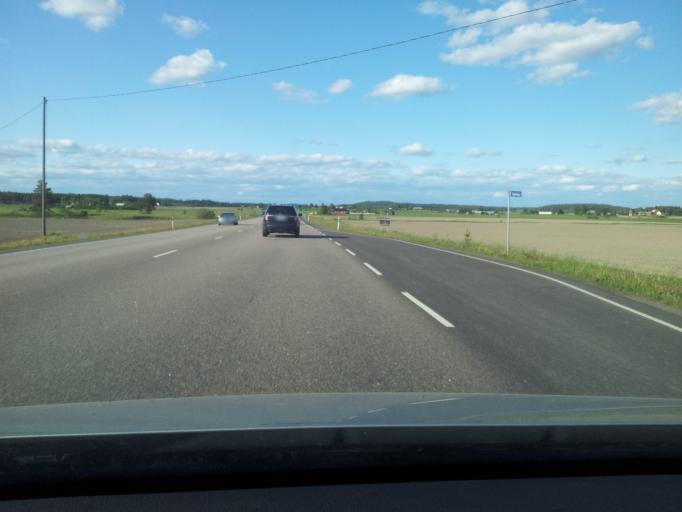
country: FI
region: Kymenlaakso
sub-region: Kouvola
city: Elimaeki
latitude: 60.7388
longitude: 26.4443
